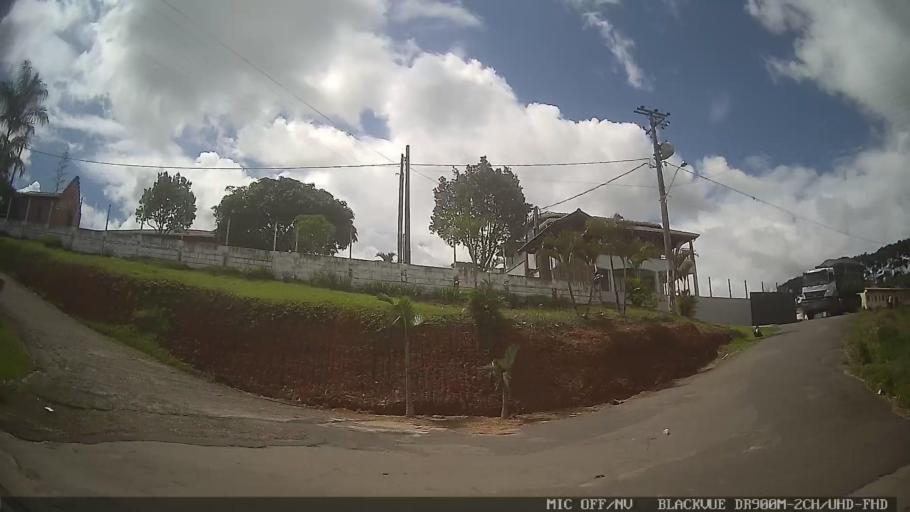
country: BR
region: Minas Gerais
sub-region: Extrema
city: Extrema
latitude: -22.8042
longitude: -46.4496
